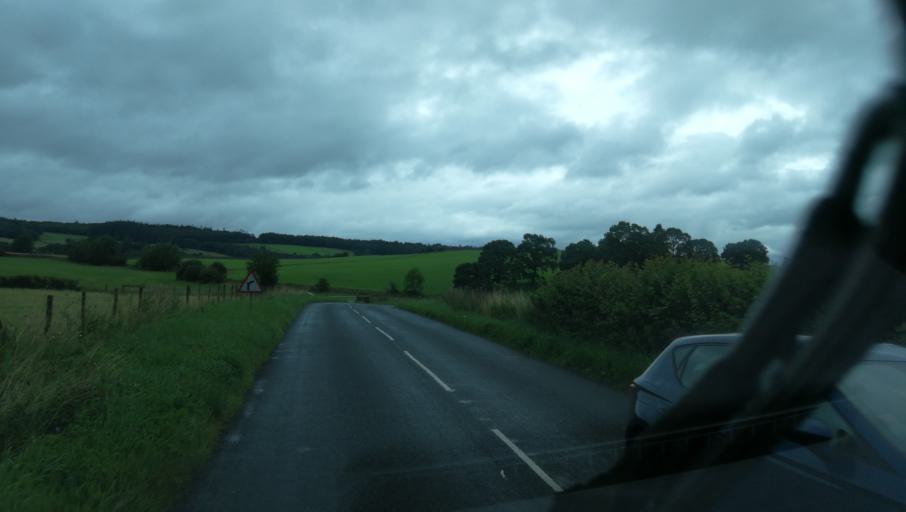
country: GB
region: England
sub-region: Cumbria
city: Penrith
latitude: 54.6228
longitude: -2.8225
